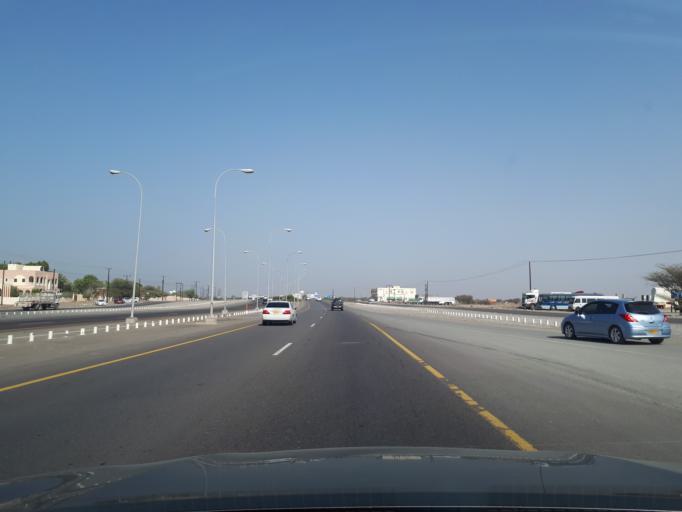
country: OM
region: Al Batinah
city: Al Sohar
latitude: 24.4143
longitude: 56.6311
